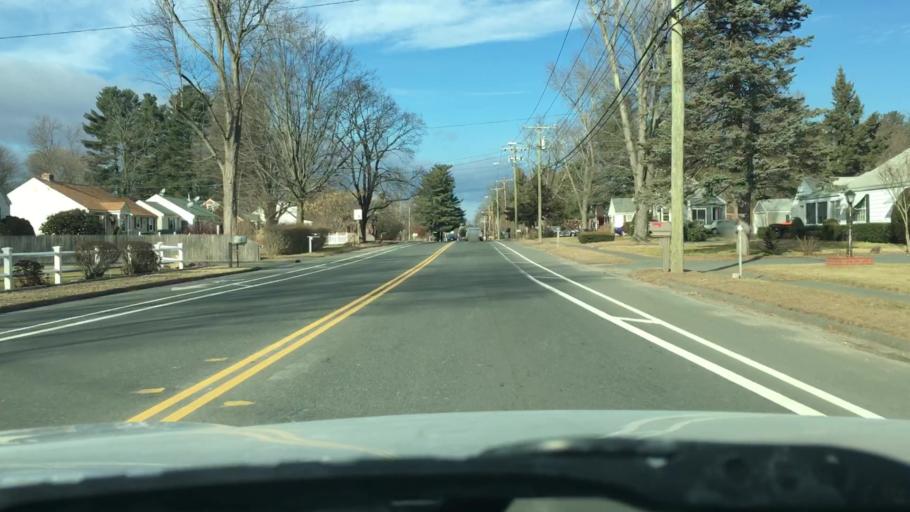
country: US
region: Massachusetts
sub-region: Hampden County
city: Agawam
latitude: 42.0633
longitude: -72.6319
